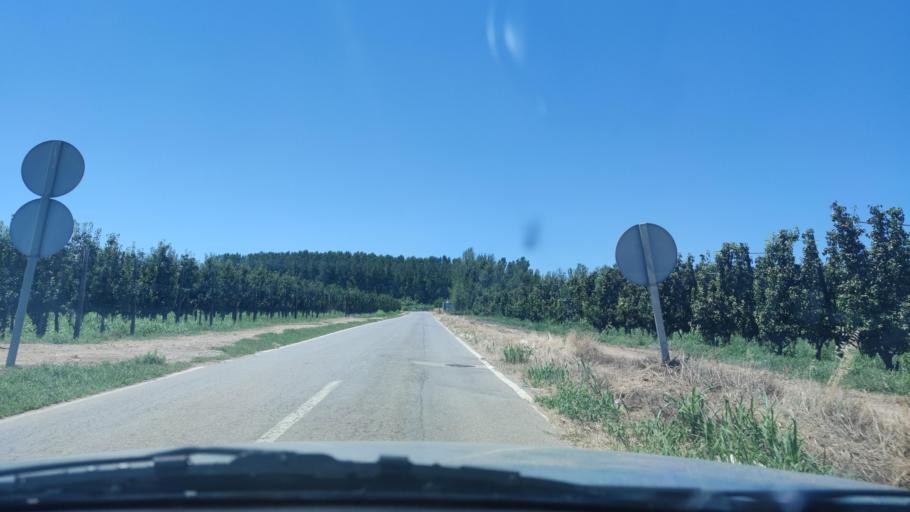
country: ES
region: Catalonia
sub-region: Provincia de Lleida
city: Alcoletge
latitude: 41.6549
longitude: 0.6832
